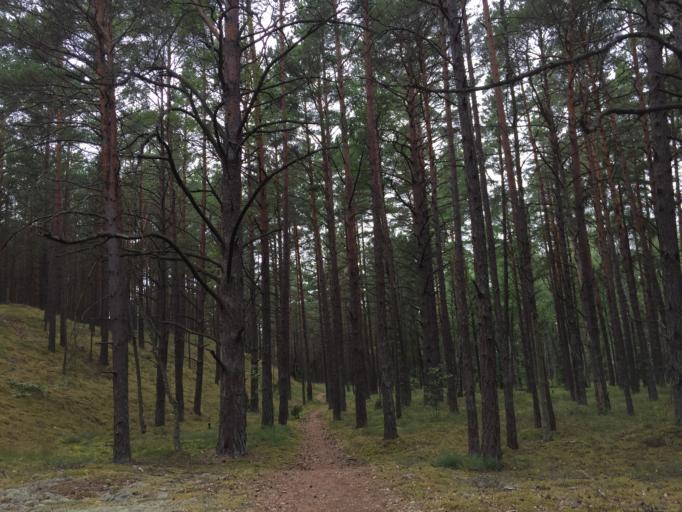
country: LV
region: Riga
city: Jaunciems
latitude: 57.1043
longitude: 24.1777
